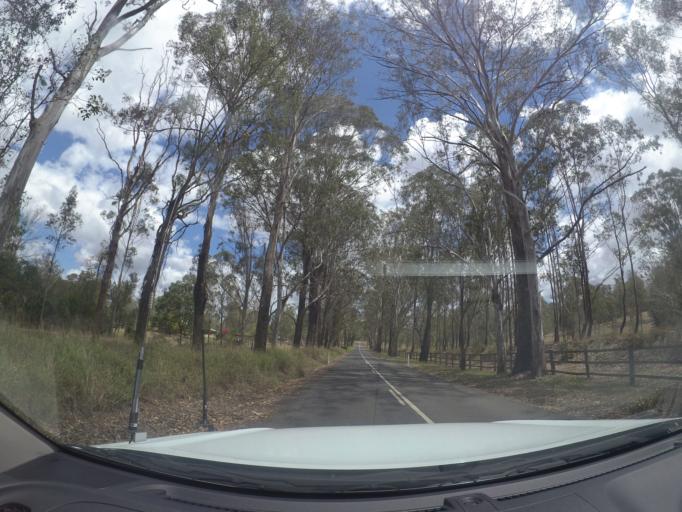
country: AU
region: Queensland
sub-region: Logan
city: Cedar Vale
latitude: -27.9370
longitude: 153.0700
